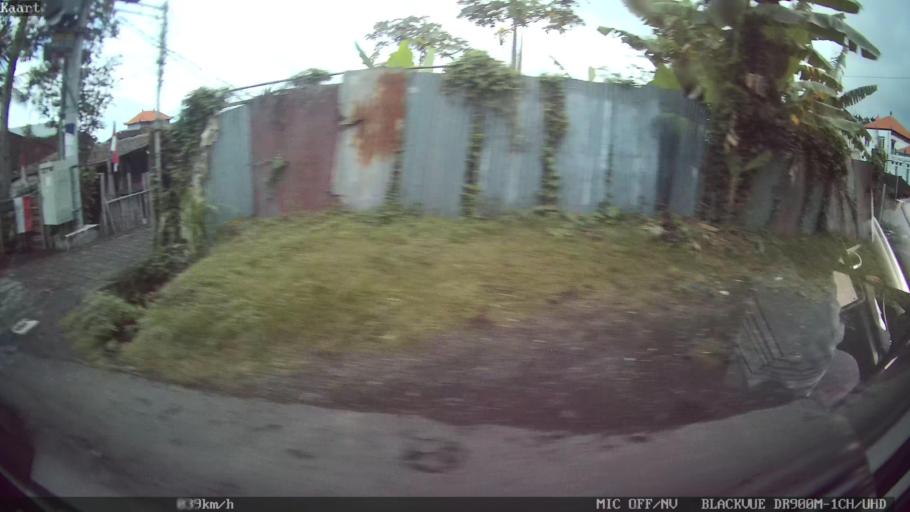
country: ID
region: Bali
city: Banjar Keraman
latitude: -8.5390
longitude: 115.2143
